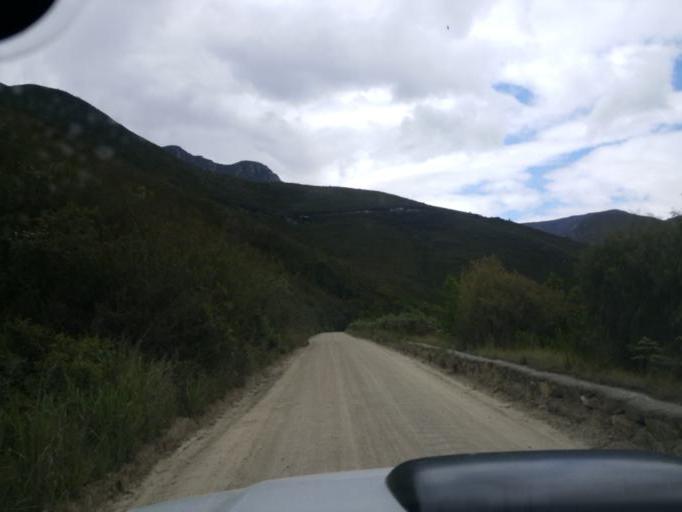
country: ZA
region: Western Cape
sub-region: Eden District Municipality
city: George
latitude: -33.9180
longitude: 22.4159
